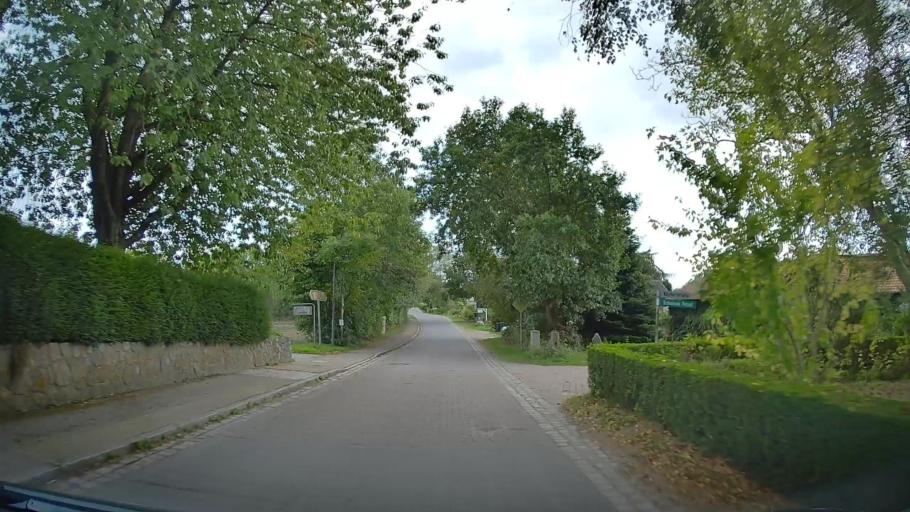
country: DE
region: Schleswig-Holstein
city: Steinberg
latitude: 54.7732
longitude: 9.8035
